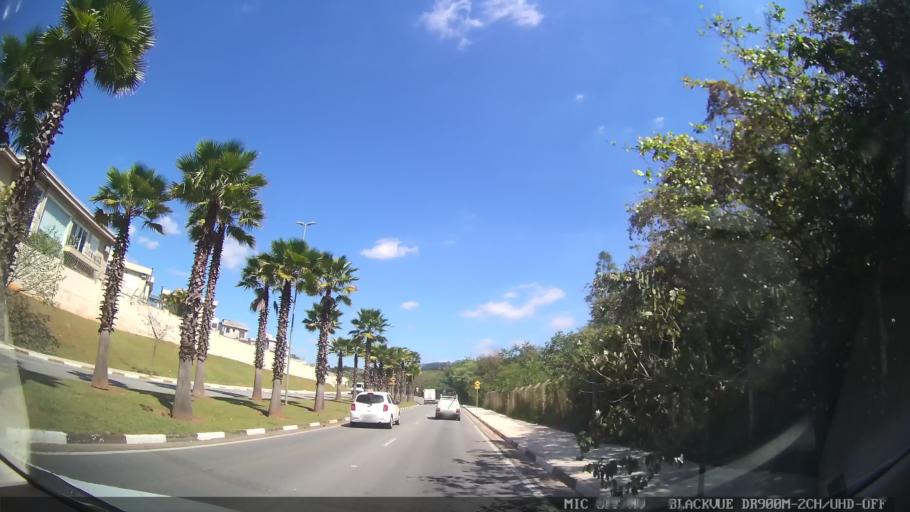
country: BR
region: Sao Paulo
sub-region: Santana De Parnaiba
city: Santana de Parnaiba
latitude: -23.4368
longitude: -46.8324
